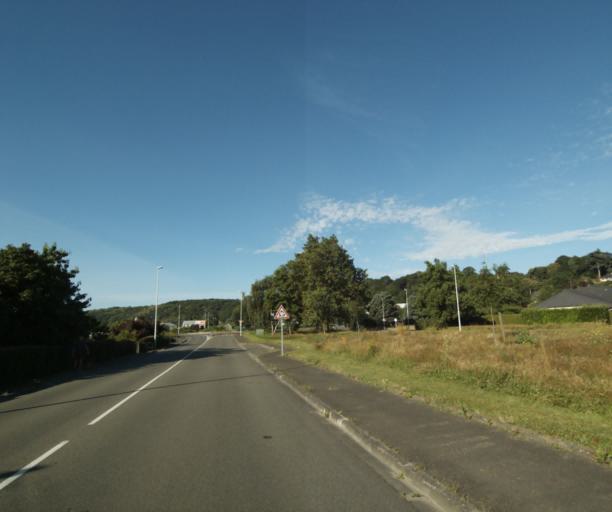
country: FR
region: Pays de la Loire
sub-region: Departement de la Mayenne
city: Laval
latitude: 48.0535
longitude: -0.7625
